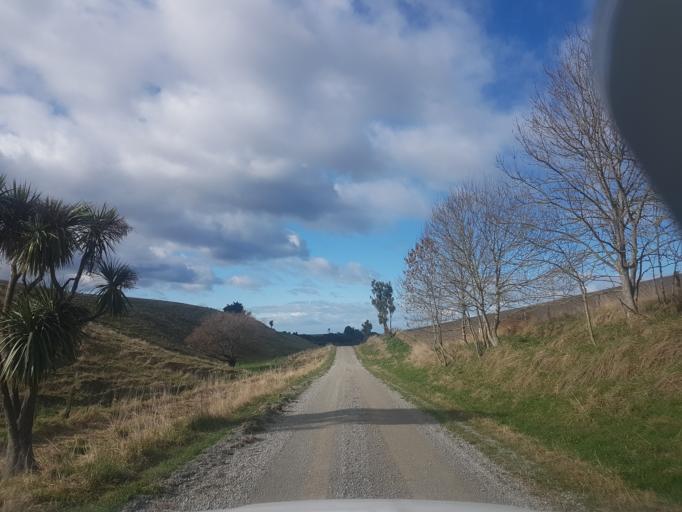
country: NZ
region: Canterbury
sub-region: Timaru District
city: Pleasant Point
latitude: -44.1834
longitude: 171.1312
